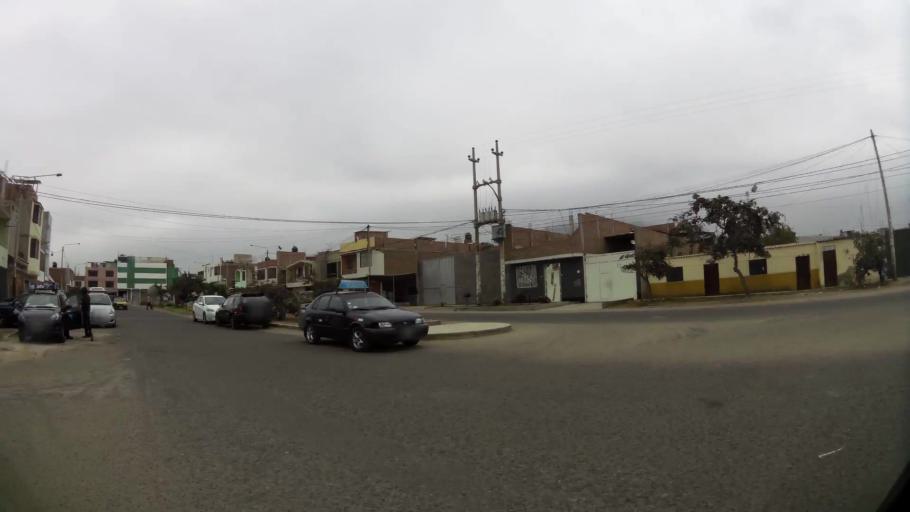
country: PE
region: La Libertad
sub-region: Provincia de Trujillo
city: La Esperanza
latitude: -8.0744
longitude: -79.0532
